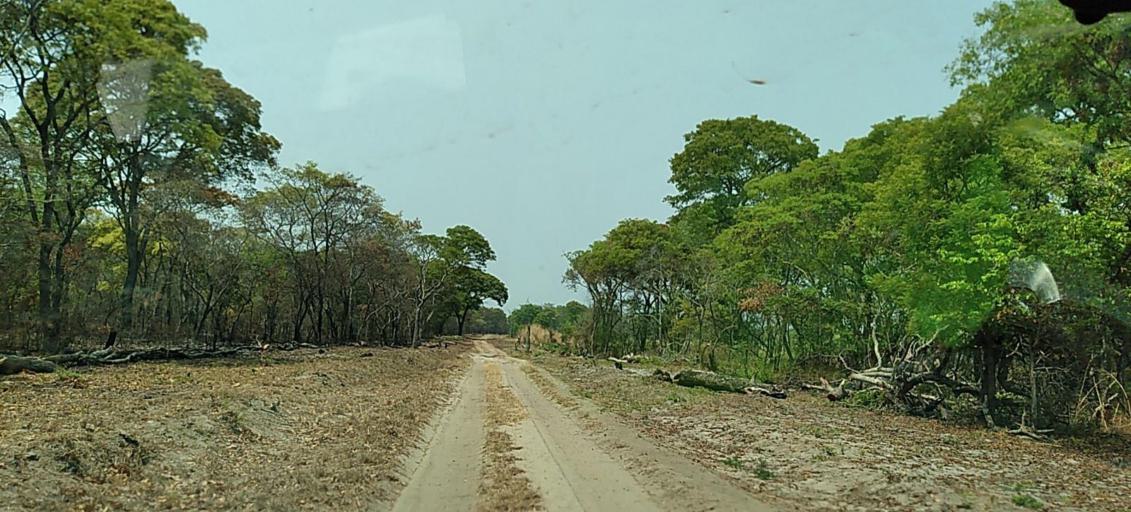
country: ZM
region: Western
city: Lukulu
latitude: -13.9530
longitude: 23.2244
